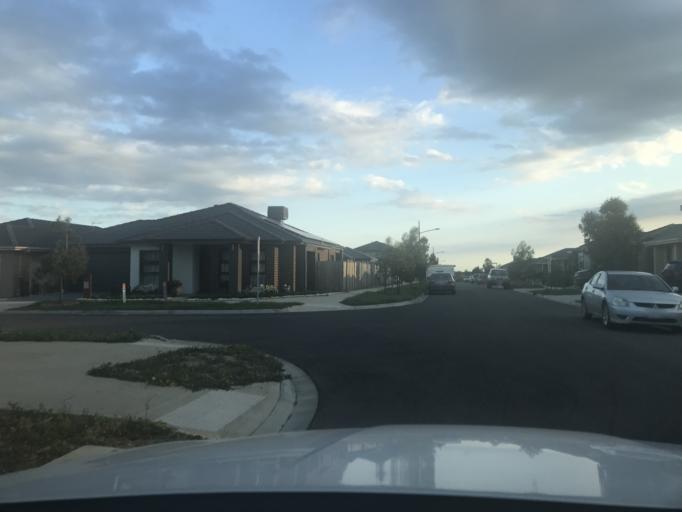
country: AU
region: Victoria
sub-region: Hume
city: Greenvale
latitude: -37.5731
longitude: 144.8889
